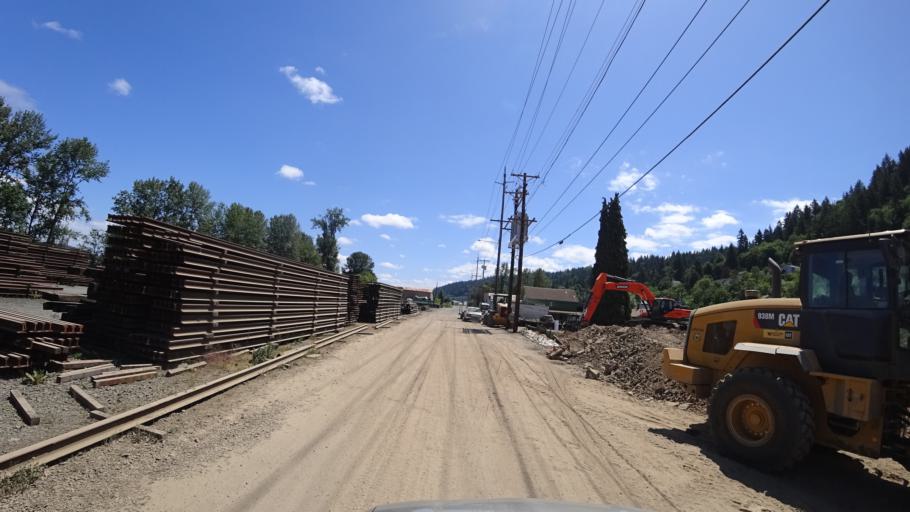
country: US
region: Oregon
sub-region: Washington County
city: Cedar Mill
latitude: 45.6022
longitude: -122.7866
